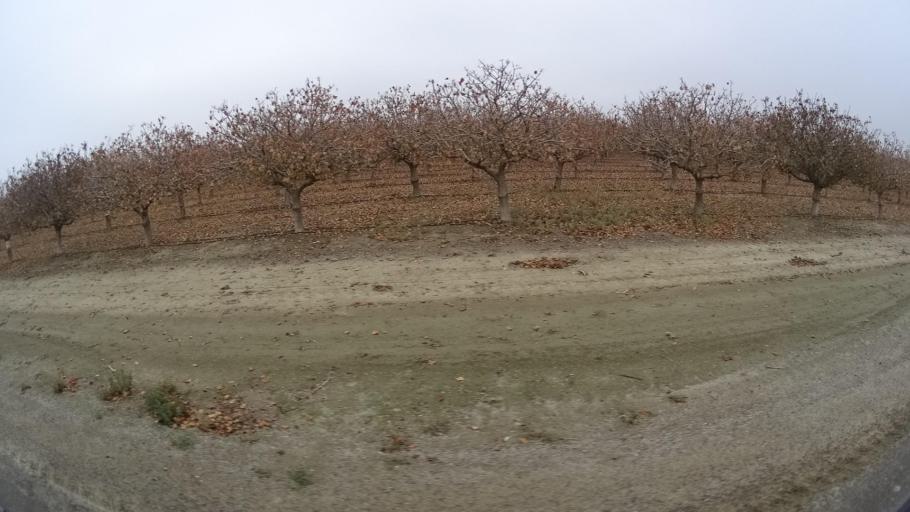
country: US
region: California
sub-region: Kern County
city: Wasco
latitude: 35.6976
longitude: -119.4906
